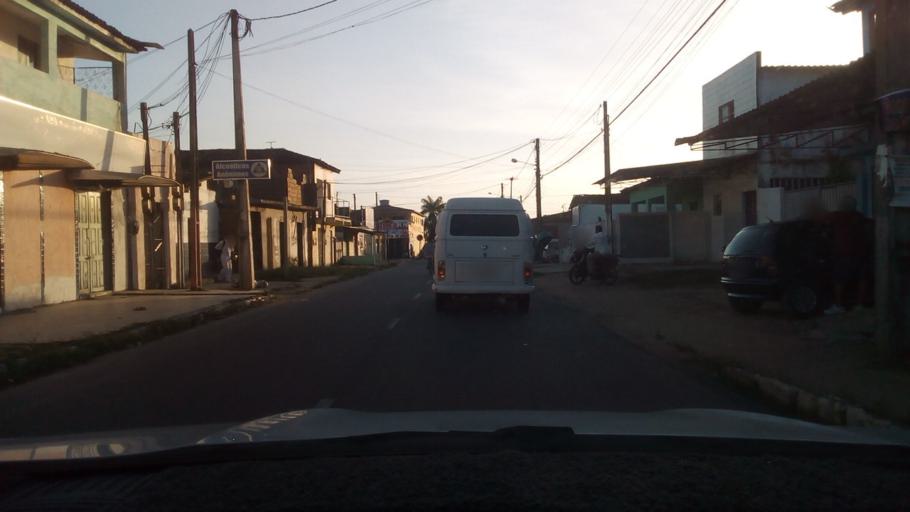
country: BR
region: Paraiba
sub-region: Bayeux
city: Bayeux
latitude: -7.1785
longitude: -34.9210
